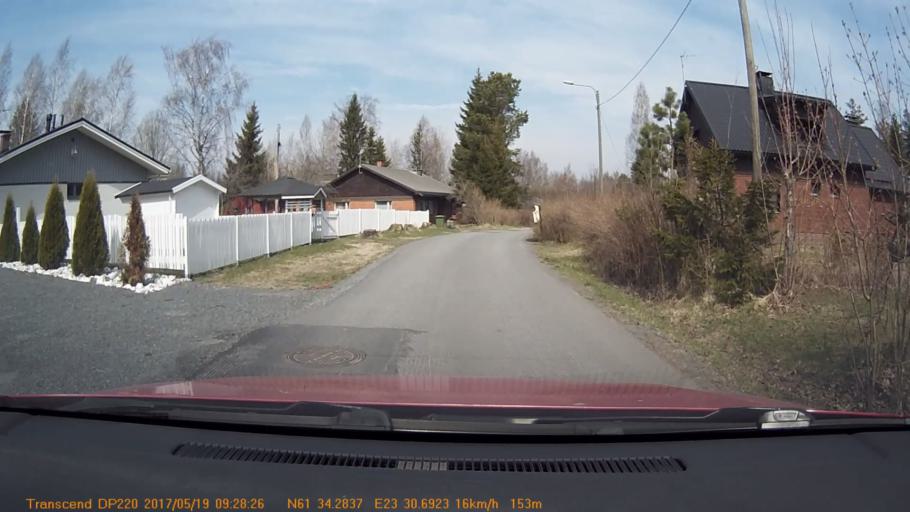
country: FI
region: Pirkanmaa
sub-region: Tampere
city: Yloejaervi
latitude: 61.5714
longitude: 23.5116
